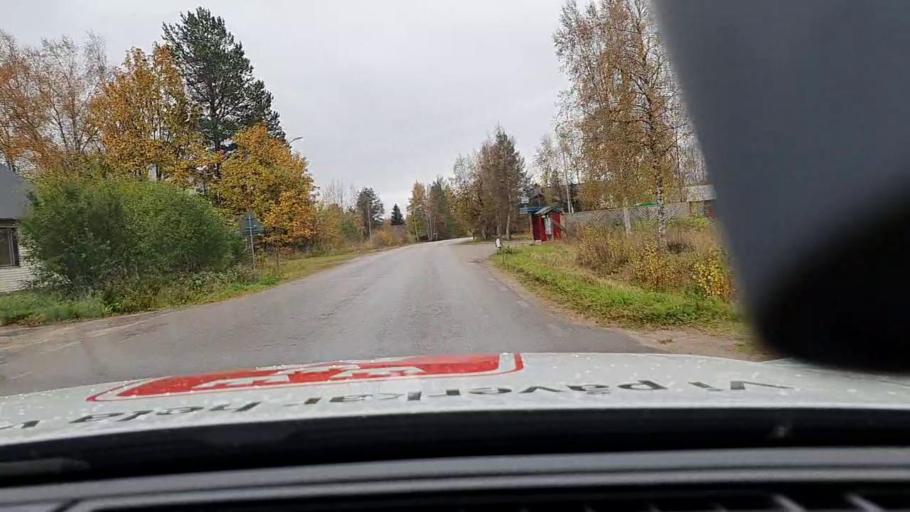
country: SE
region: Norrbotten
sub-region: Haparanda Kommun
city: Haparanda
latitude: 65.8043
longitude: 23.9178
